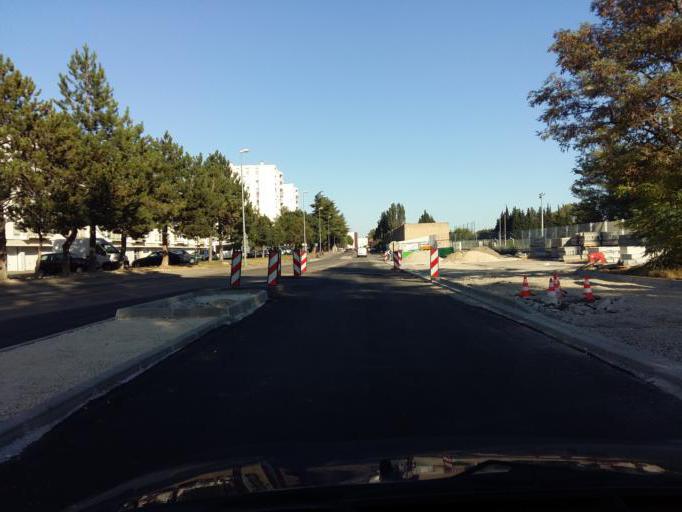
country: FR
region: Provence-Alpes-Cote d'Azur
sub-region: Departement du Vaucluse
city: Montfavet
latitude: 43.9305
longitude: 4.8414
